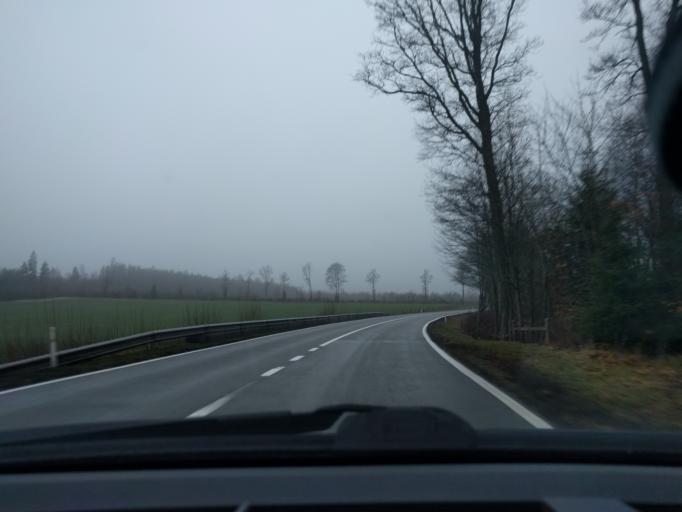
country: BE
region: Wallonia
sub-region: Province du Luxembourg
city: Gouvy
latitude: 50.2194
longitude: 5.9713
